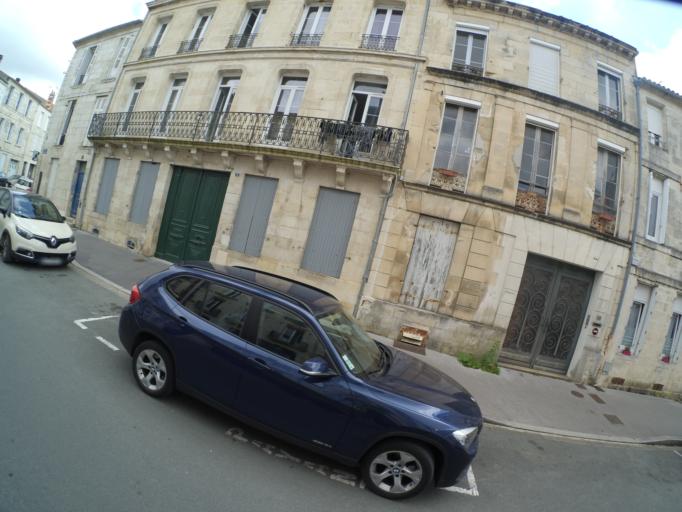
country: FR
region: Poitou-Charentes
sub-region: Departement de la Charente-Maritime
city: Rochefort
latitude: 45.9397
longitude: -0.9604
